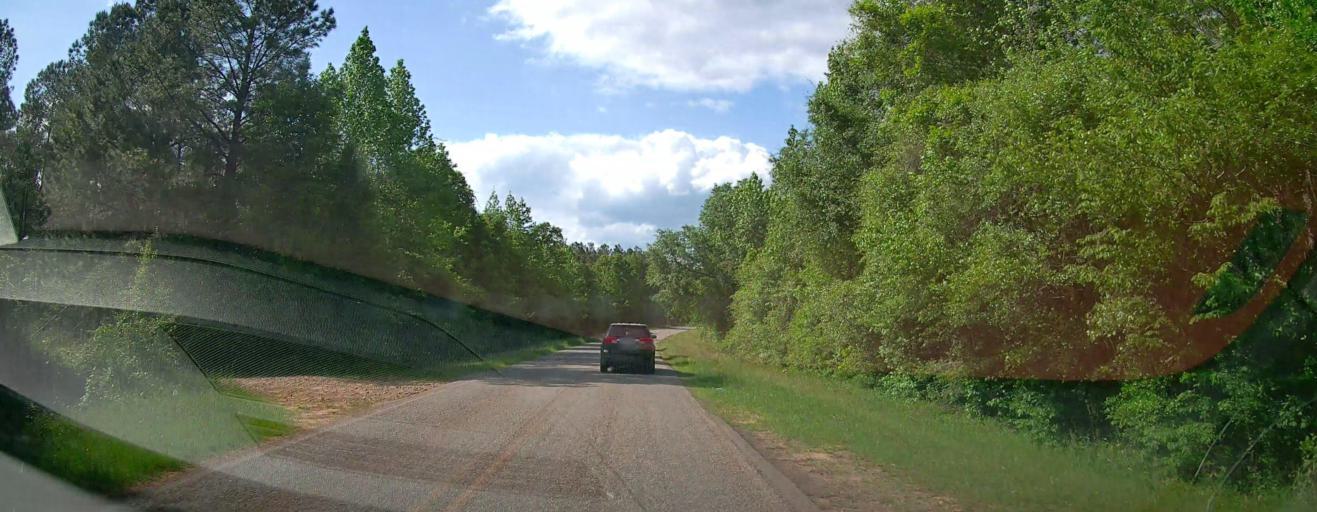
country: US
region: Georgia
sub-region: Laurens County
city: East Dublin
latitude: 32.7040
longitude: -82.9170
